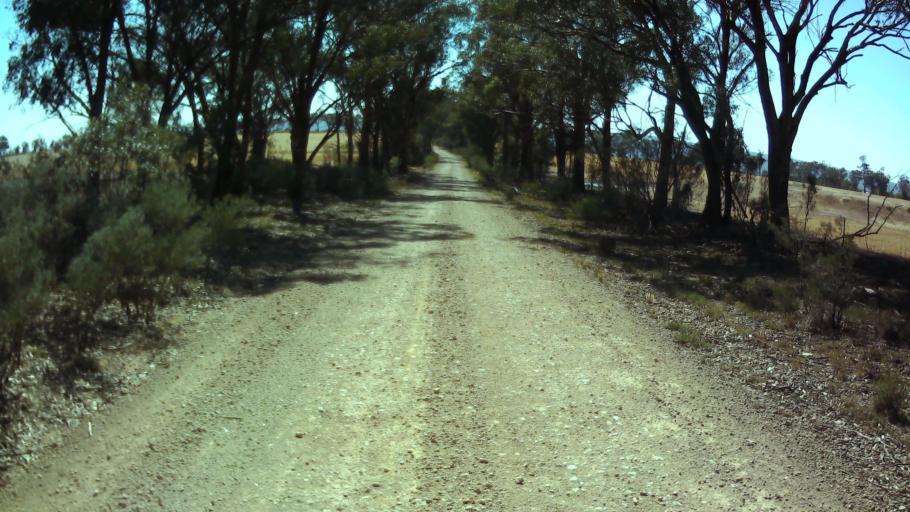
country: AU
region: New South Wales
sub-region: Weddin
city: Grenfell
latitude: -33.9017
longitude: 147.8717
